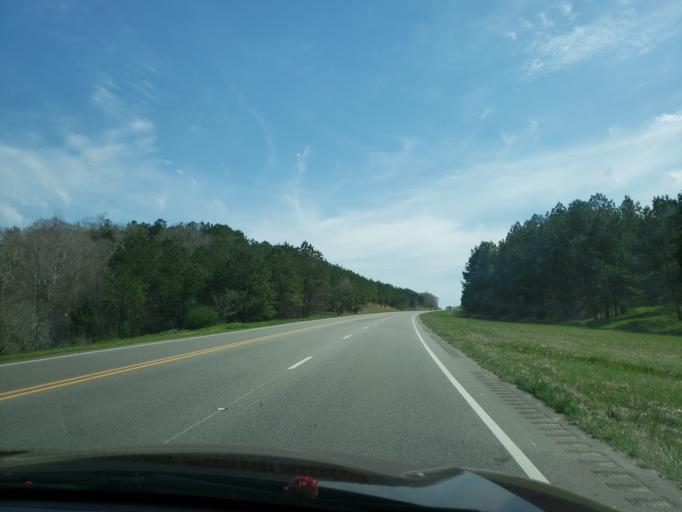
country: US
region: Alabama
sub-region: Autauga County
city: Prattville
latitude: 32.4328
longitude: -86.5623
